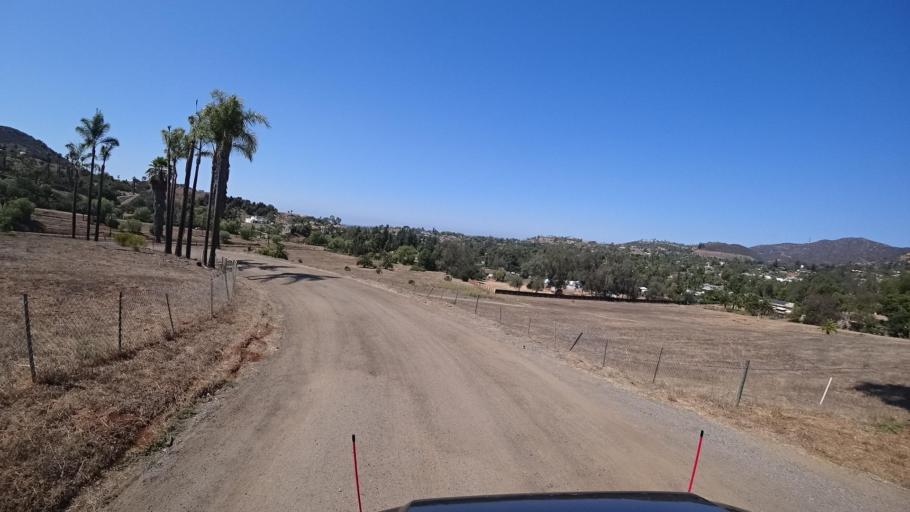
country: US
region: California
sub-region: San Diego County
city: San Marcos
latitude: 33.1877
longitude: -117.1803
